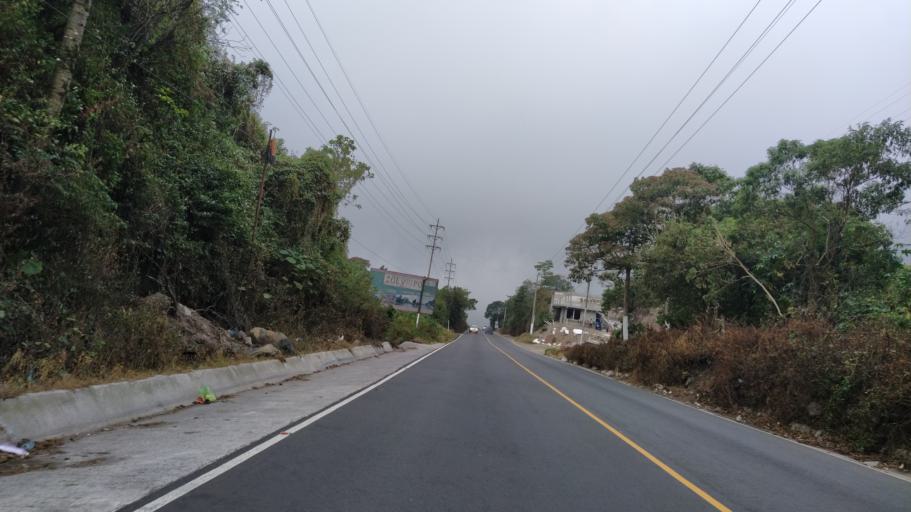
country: GT
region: Quetzaltenango
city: Zunil
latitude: 14.7376
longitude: -91.5207
